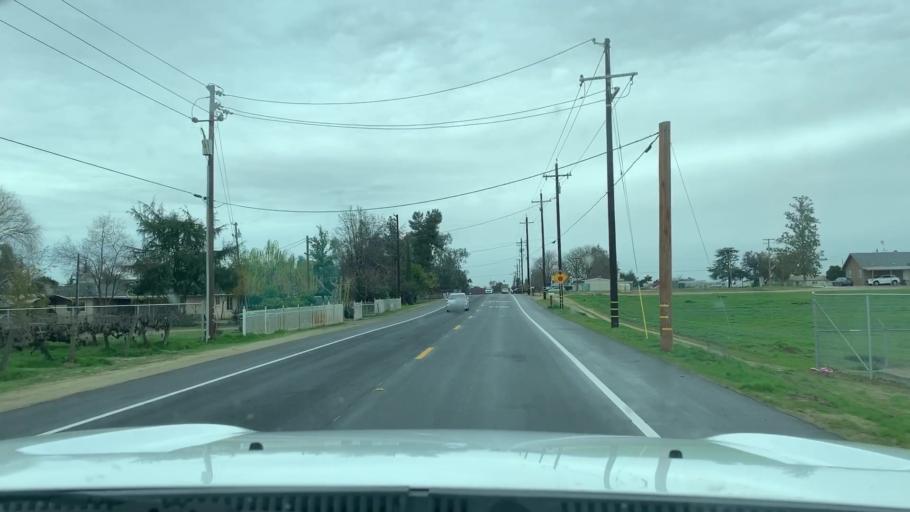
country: US
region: California
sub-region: Fresno County
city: Fowler
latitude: 36.5743
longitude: -119.6825
